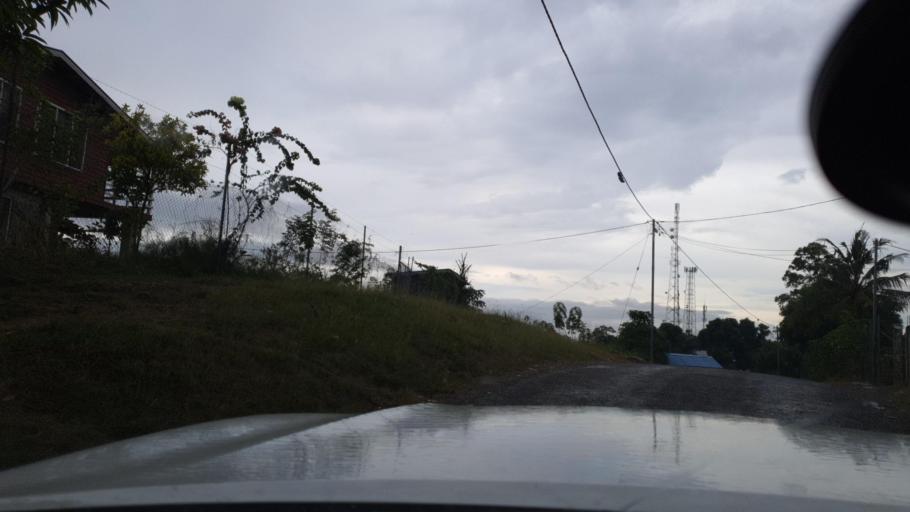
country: SB
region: Guadalcanal
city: Honiara
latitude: -9.4416
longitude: 159.9483
